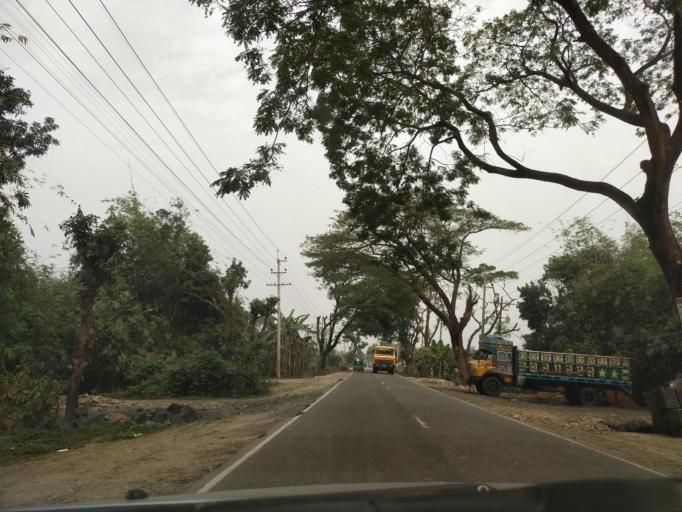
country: BD
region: Dhaka
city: Narsingdi
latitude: 24.0088
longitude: 90.7373
